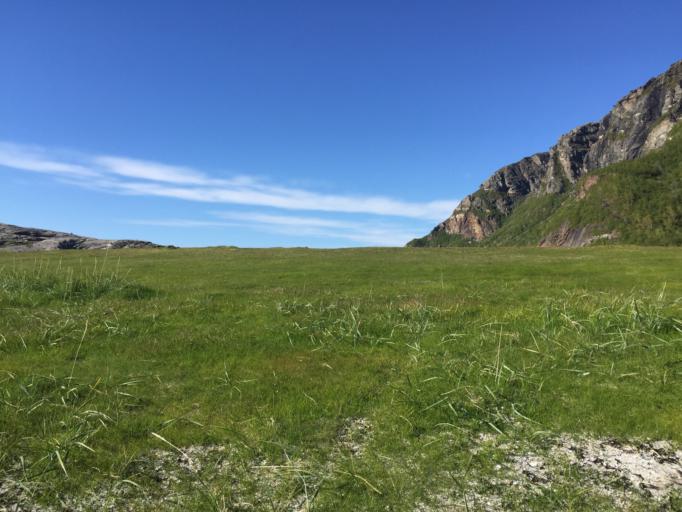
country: NO
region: Nordland
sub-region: Bodo
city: Loding
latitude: 67.4192
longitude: 14.6313
